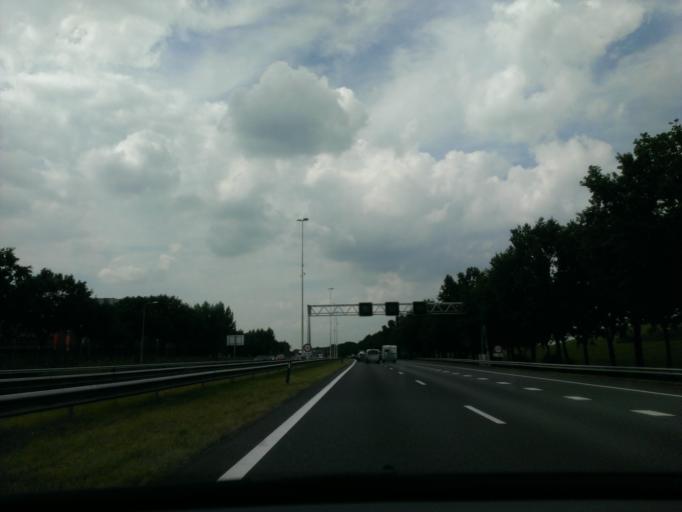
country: NL
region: Utrecht
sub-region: Gemeente Amersfoort
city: Hoogland
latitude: 52.1992
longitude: 5.3959
